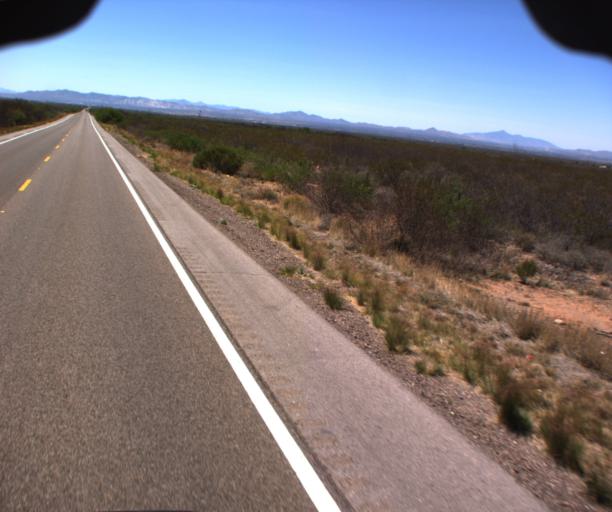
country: US
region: Arizona
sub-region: Cochise County
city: Douglas
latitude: 31.4349
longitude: -109.4807
